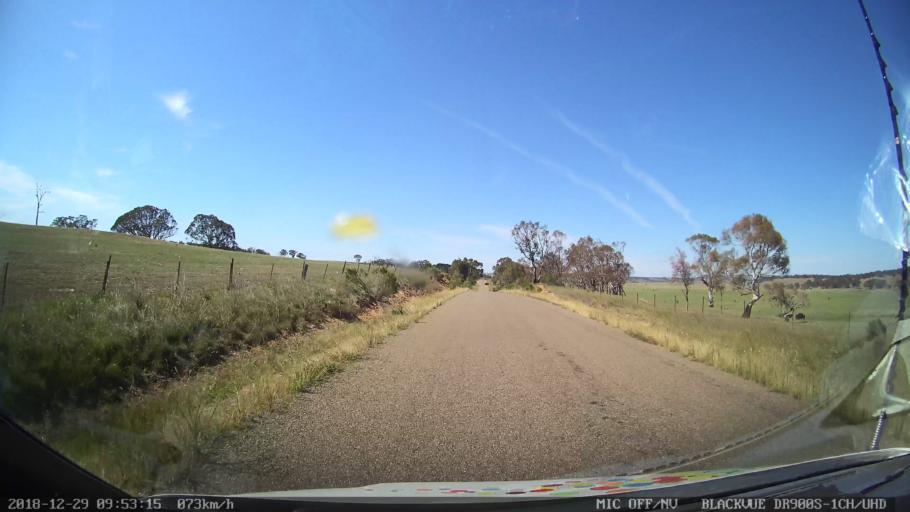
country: AU
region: New South Wales
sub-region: Goulburn Mulwaree
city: Goulburn
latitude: -34.7496
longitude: 149.4698
